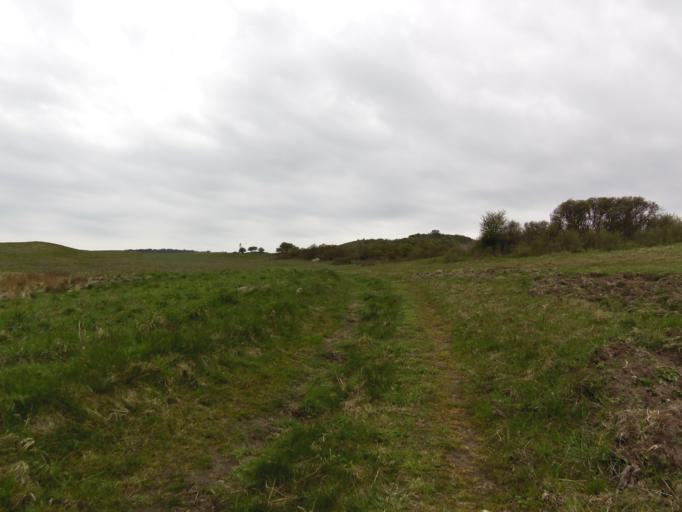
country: DE
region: Mecklenburg-Vorpommern
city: Hiddensee
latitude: 54.6021
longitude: 13.1379
